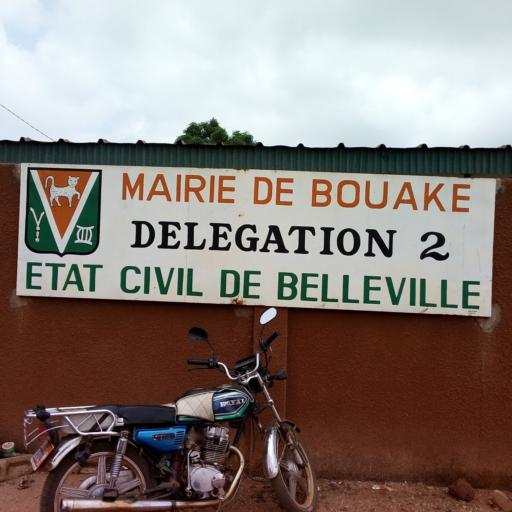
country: CI
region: Vallee du Bandama
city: Bouake
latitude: 7.7160
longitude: -5.0012
